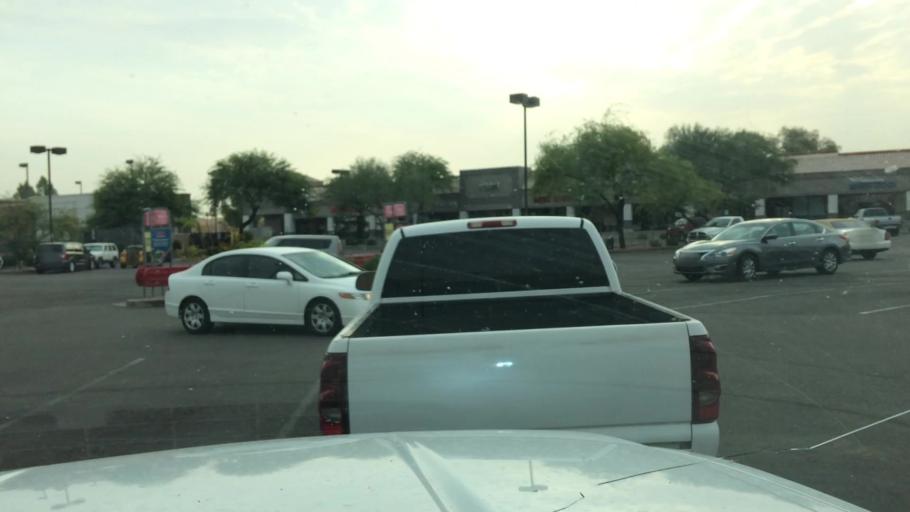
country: US
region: Arizona
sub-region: Maricopa County
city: Peoria
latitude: 33.5652
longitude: -112.2540
